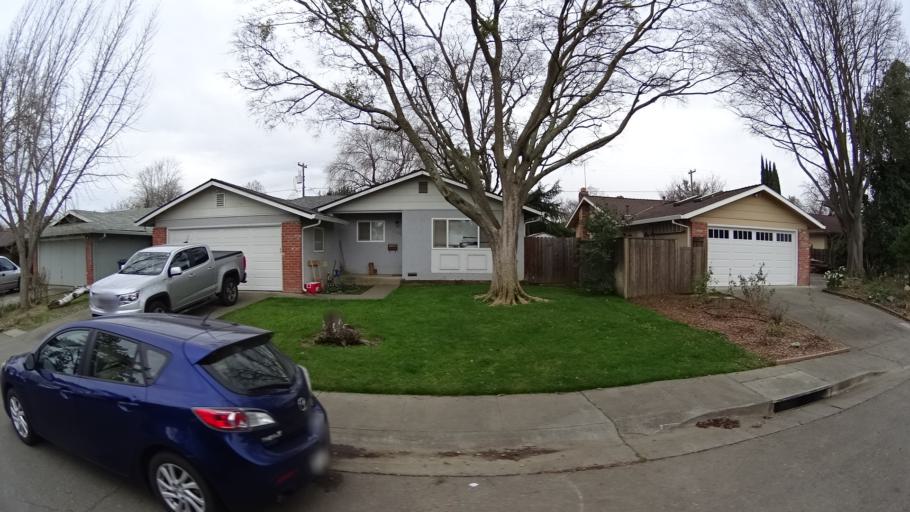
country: US
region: California
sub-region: Yolo County
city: Davis
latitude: 38.5607
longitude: -121.7229
